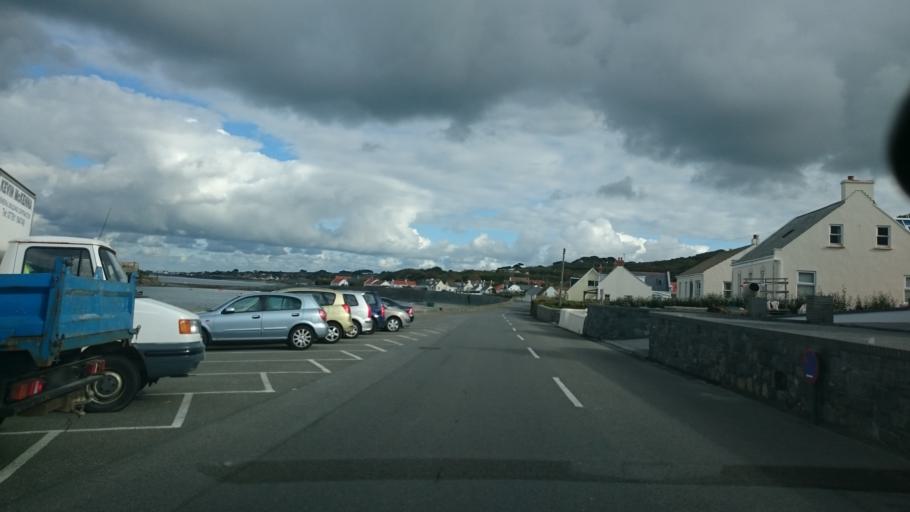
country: GG
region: St Peter Port
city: Saint Peter Port
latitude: 49.4349
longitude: -2.6566
